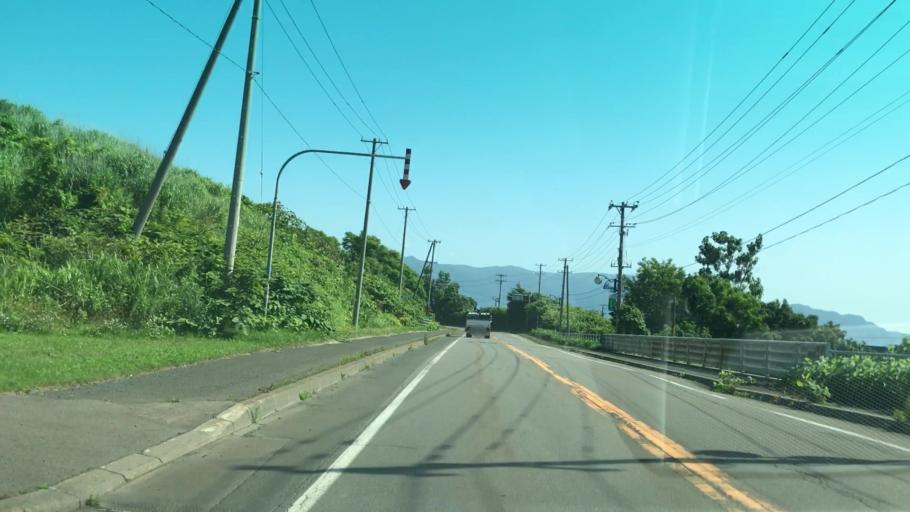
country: JP
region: Hokkaido
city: Iwanai
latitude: 43.0615
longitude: 140.4973
